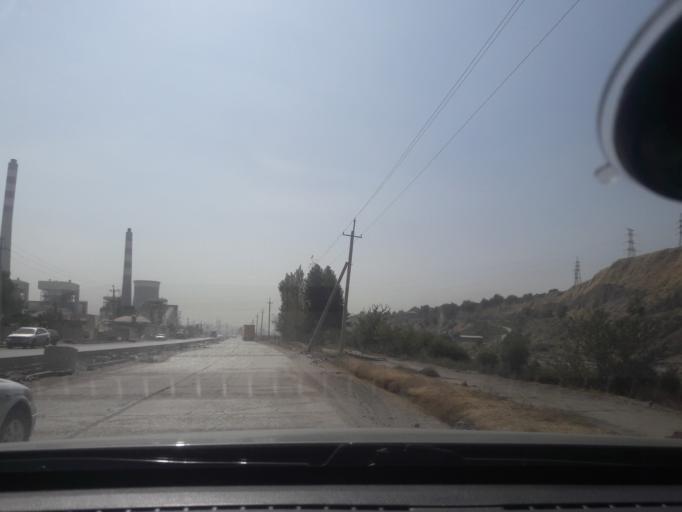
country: TJ
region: Dushanbe
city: Dushanbe
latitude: 38.6163
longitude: 68.7685
